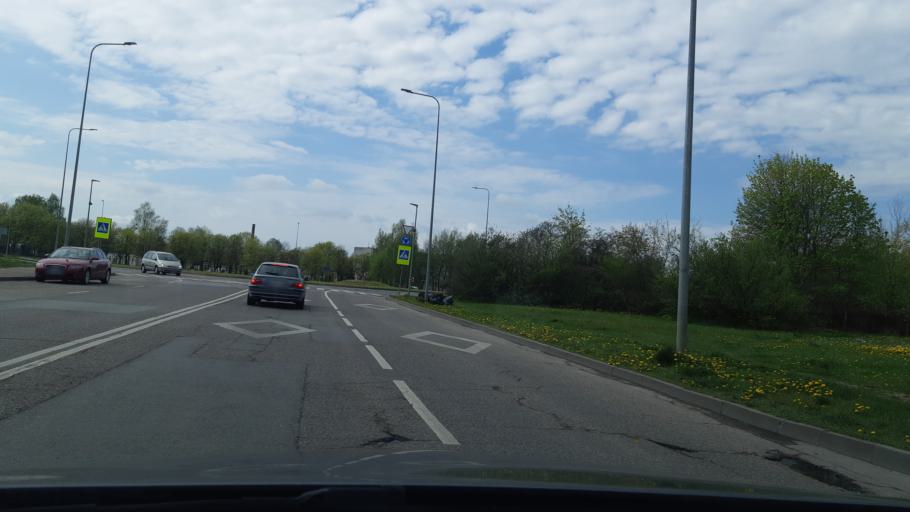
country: LT
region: Kauno apskritis
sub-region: Kaunas
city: Silainiai
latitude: 54.9170
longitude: 23.8632
